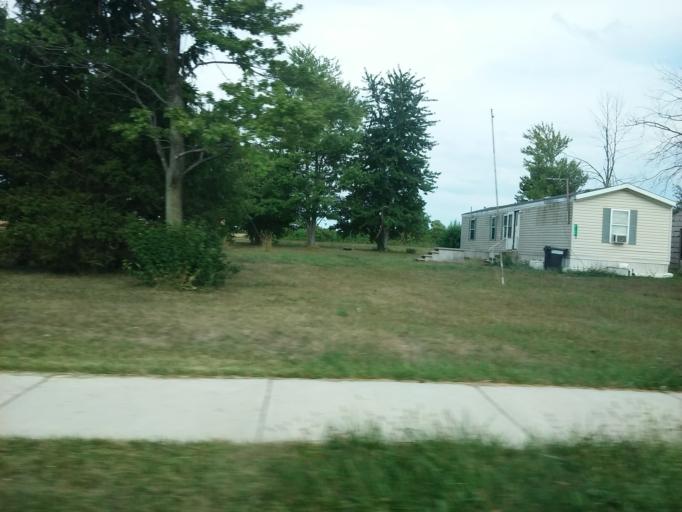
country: US
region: Ohio
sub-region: Hancock County
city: McComb
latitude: 41.1872
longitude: -83.7843
